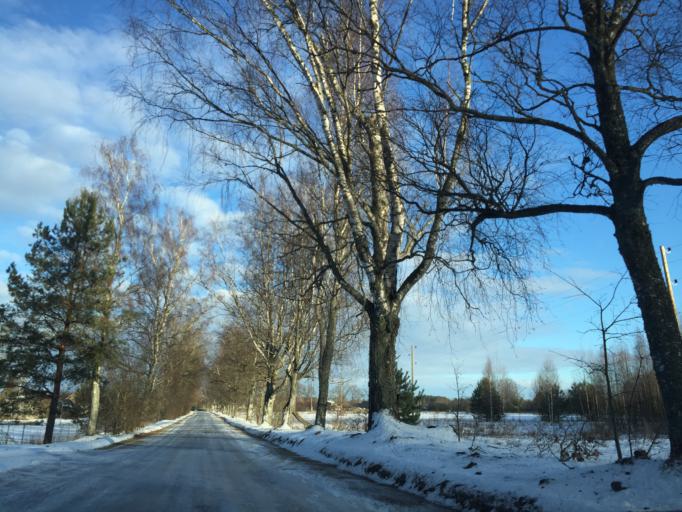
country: LV
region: Kegums
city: Kegums
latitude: 56.7410
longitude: 24.6661
